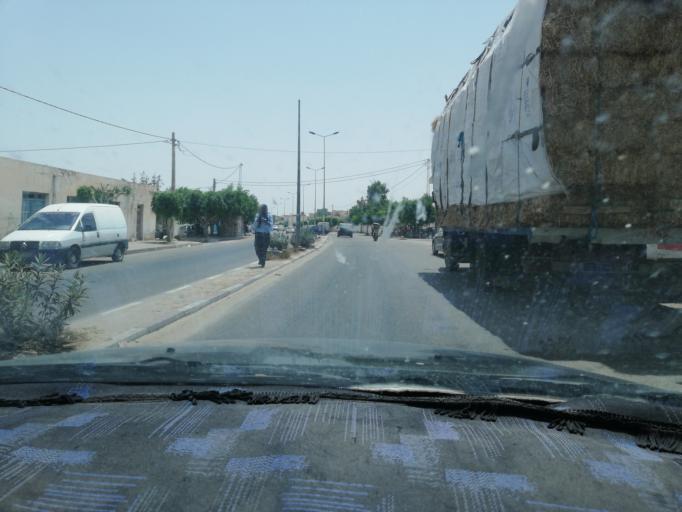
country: TN
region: Qabis
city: Gabes
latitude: 33.6206
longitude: 10.2833
